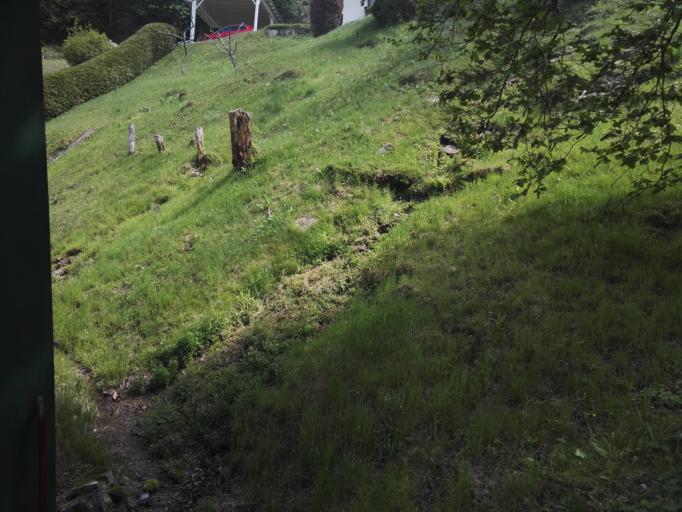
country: AT
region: Styria
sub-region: Politischer Bezirk Weiz
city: Koglhof
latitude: 47.3063
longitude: 15.6956
